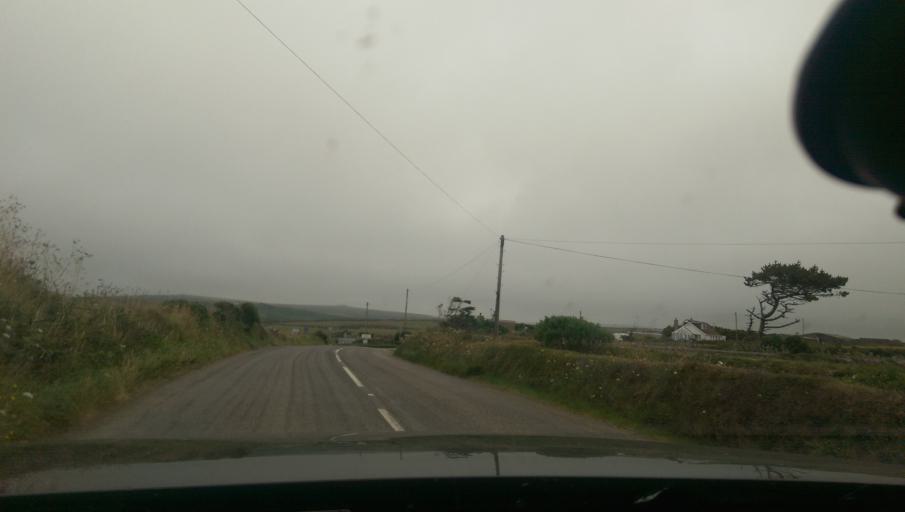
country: GB
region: England
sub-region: Cornwall
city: Saint Just
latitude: 50.1200
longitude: -5.6755
